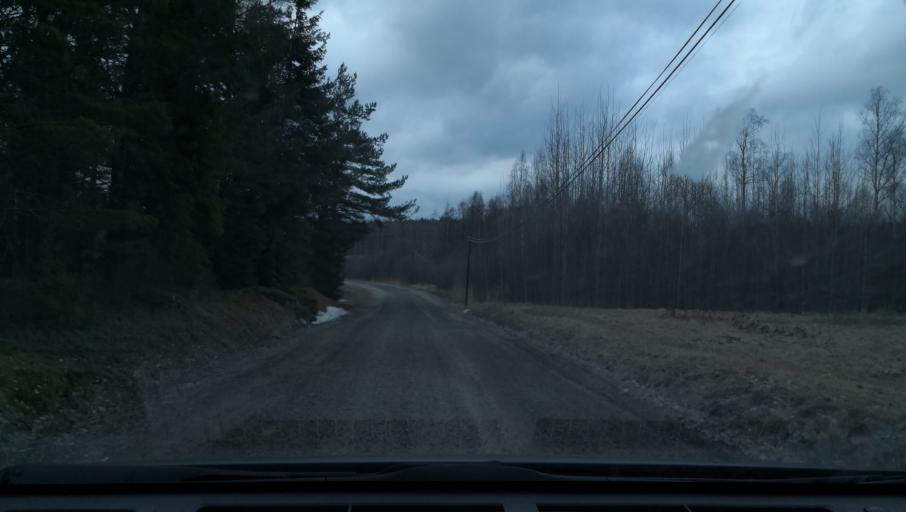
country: SE
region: Vaestmanland
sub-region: Kopings Kommun
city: Kolsva
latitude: 59.5985
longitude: 15.7134
